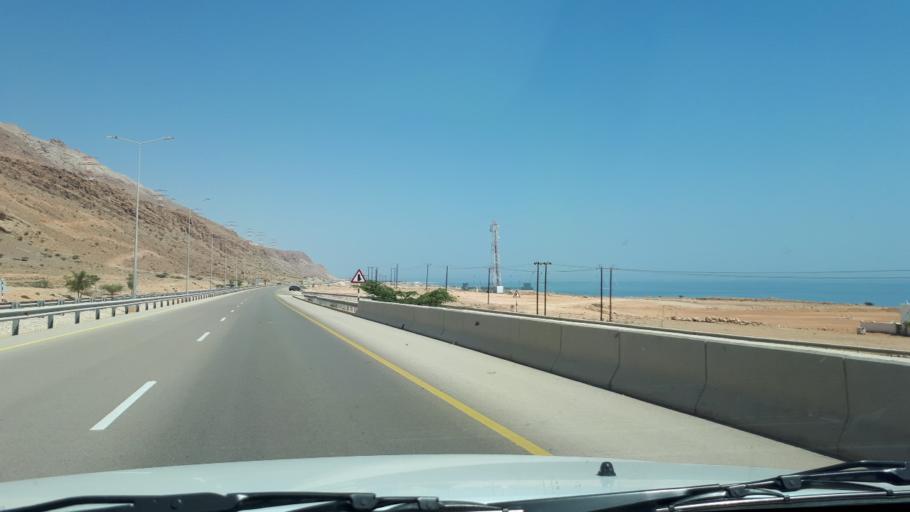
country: OM
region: Ash Sharqiyah
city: Sur
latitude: 22.7889
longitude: 59.2761
